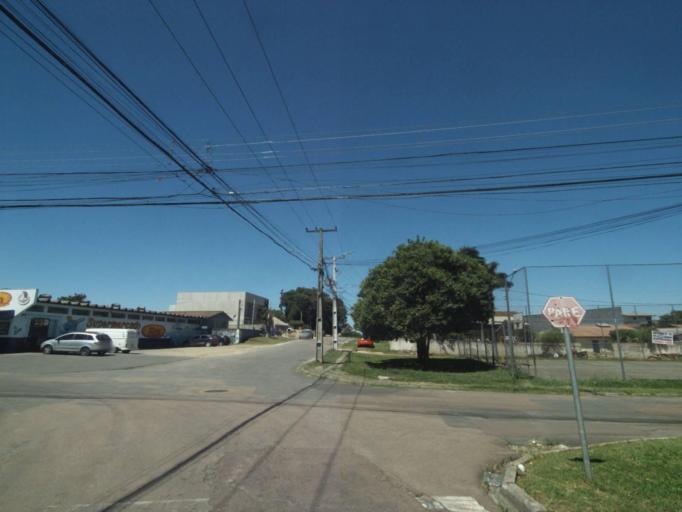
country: BR
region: Parana
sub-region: Curitiba
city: Curitiba
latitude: -25.4791
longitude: -49.3461
